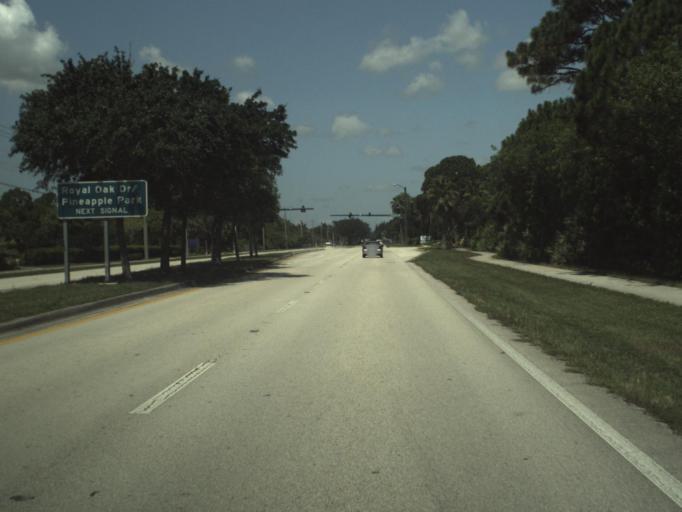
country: US
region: Florida
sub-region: Martin County
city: North River Shores
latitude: 27.2455
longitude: -80.2615
